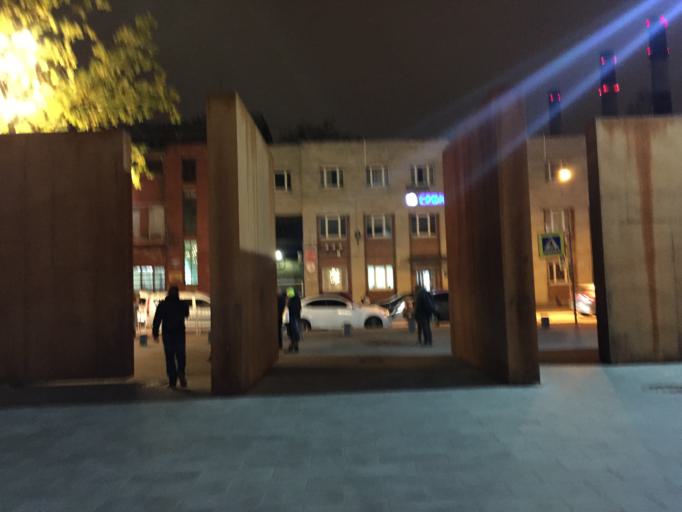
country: RU
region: St.-Petersburg
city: Vasyl'evsky Ostrov
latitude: 59.9247
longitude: 30.2413
